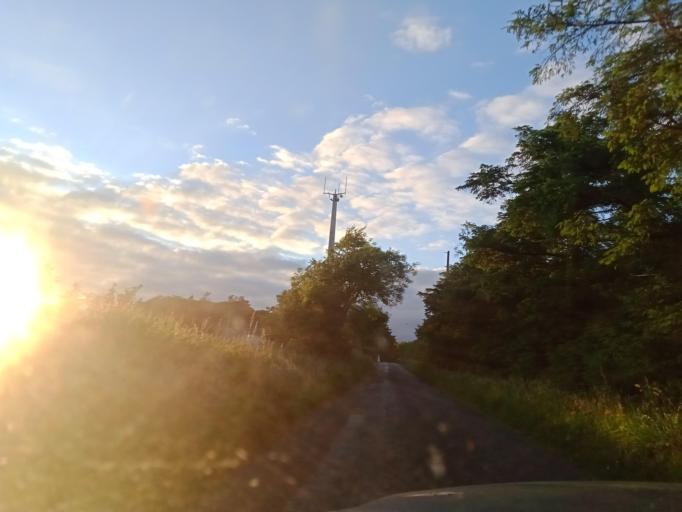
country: IE
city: Ballylinan
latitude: 52.8979
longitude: -7.1313
